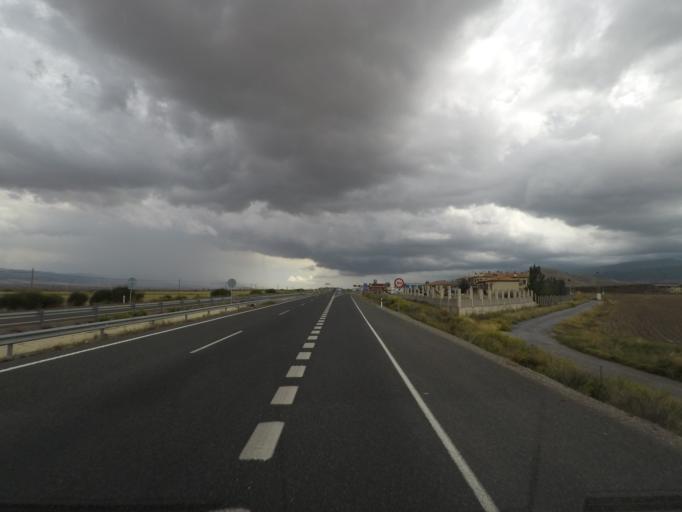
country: ES
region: Andalusia
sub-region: Provincia de Granada
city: Ferreira
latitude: 37.2074
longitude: -3.0509
